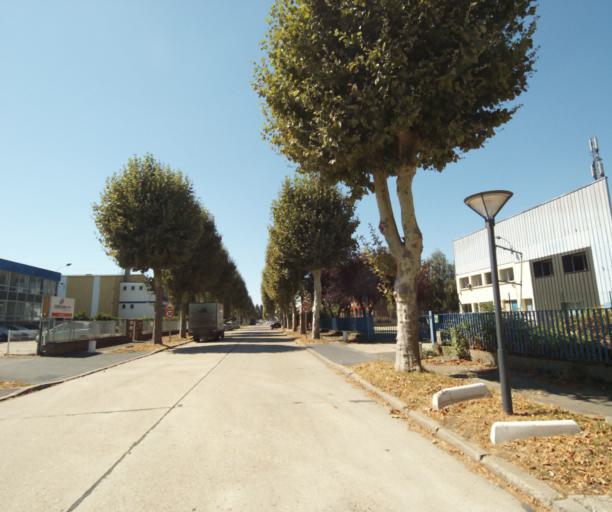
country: FR
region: Ile-de-France
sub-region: Departement des Hauts-de-Seine
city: Villeneuve-la-Garenne
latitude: 48.9446
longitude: 2.3181
